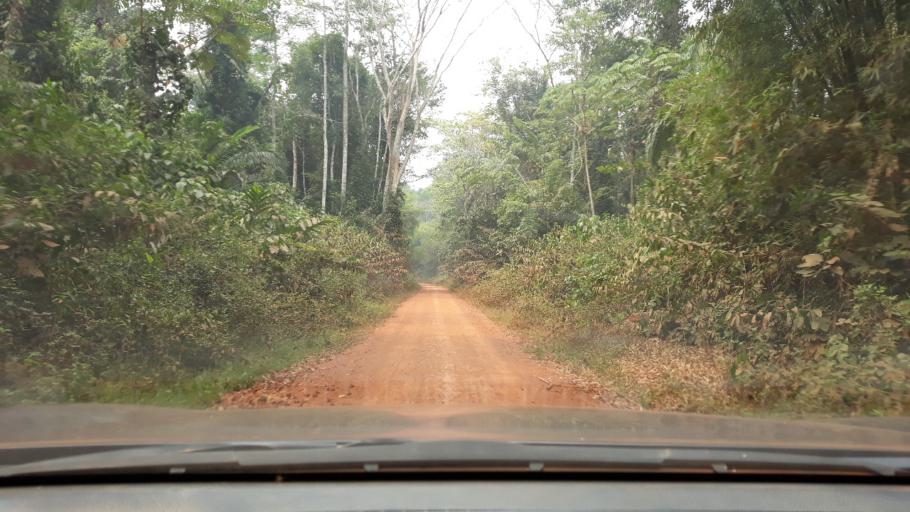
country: CD
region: Eastern Province
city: Aketi
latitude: 2.9004
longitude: 24.0394
